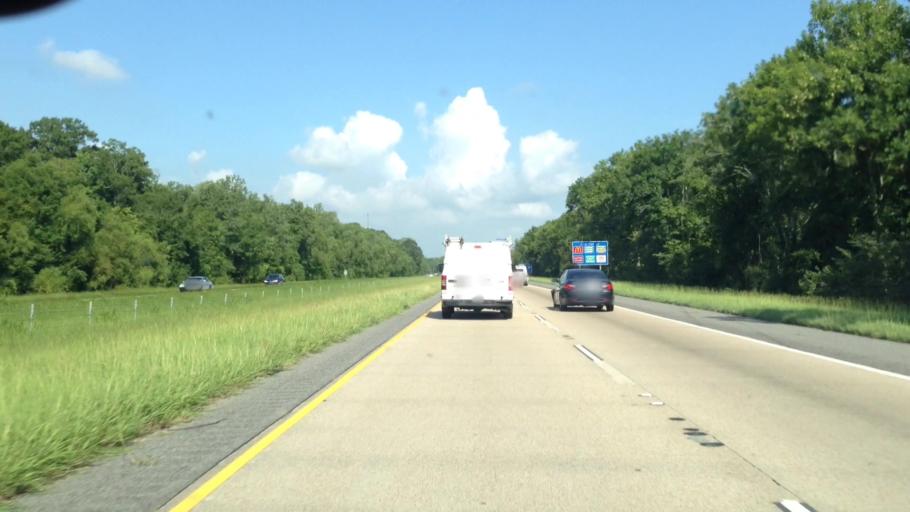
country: US
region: Louisiana
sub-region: Ascension Parish
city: Sorrento
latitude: 30.1681
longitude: -90.8642
